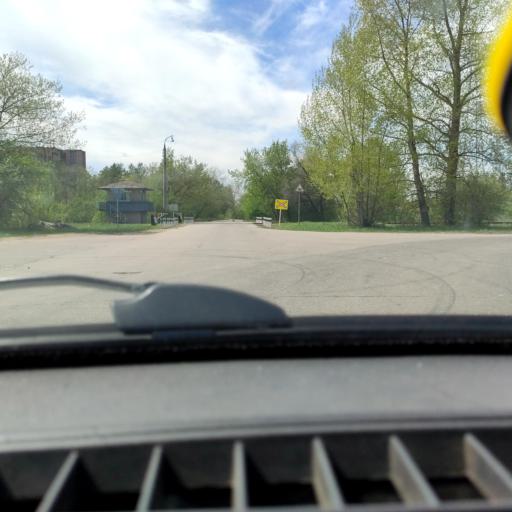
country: RU
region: Samara
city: Pribrezhnyy
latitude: 53.5164
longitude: 49.8356
